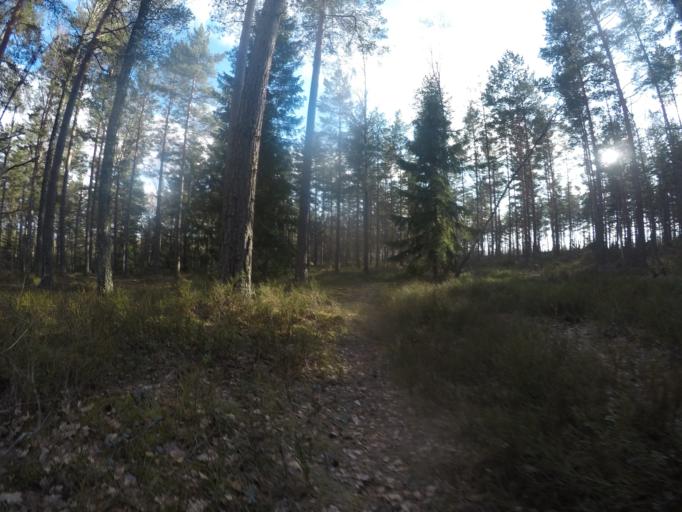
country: SE
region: Soedermanland
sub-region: Eskilstuna Kommun
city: Hallbybrunn
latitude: 59.3876
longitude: 16.4045
